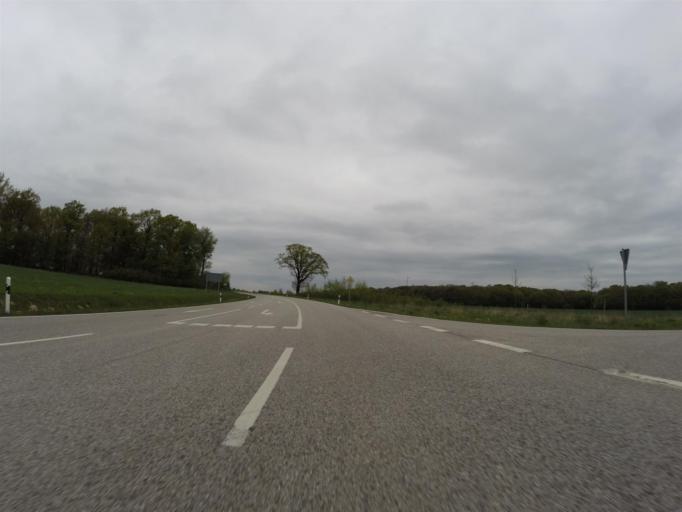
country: DE
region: Saxony-Anhalt
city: Naumburg
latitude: 51.1086
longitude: 11.7723
